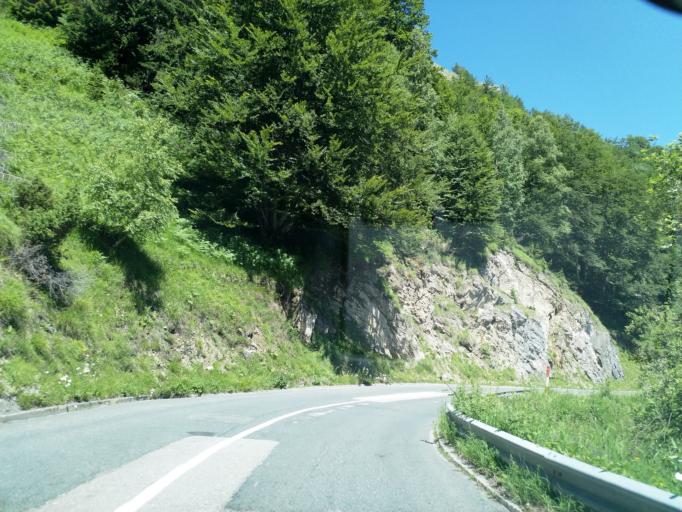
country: XK
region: Mitrovica
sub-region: Komuna e Leposaviqit
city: Leposaviq
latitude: 43.3151
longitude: 20.8555
